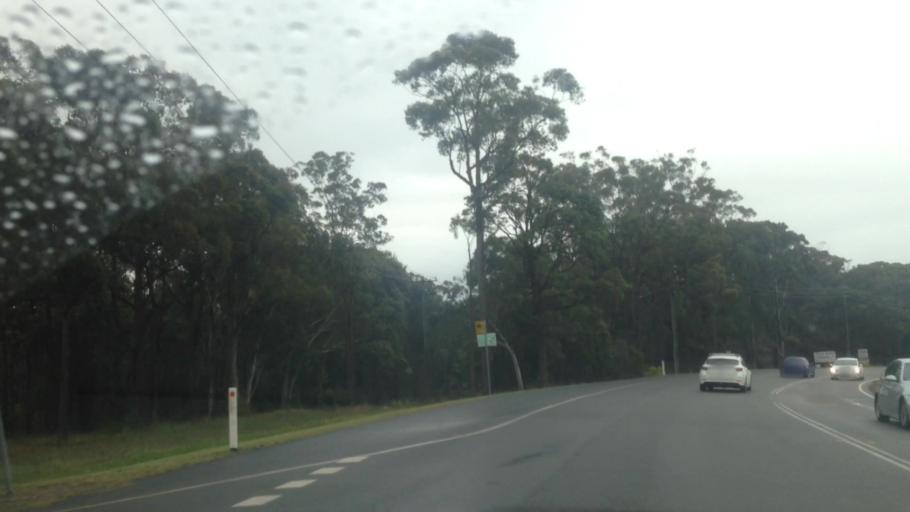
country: AU
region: New South Wales
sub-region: Wyong Shire
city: Charmhaven
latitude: -33.1680
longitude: 151.4758
